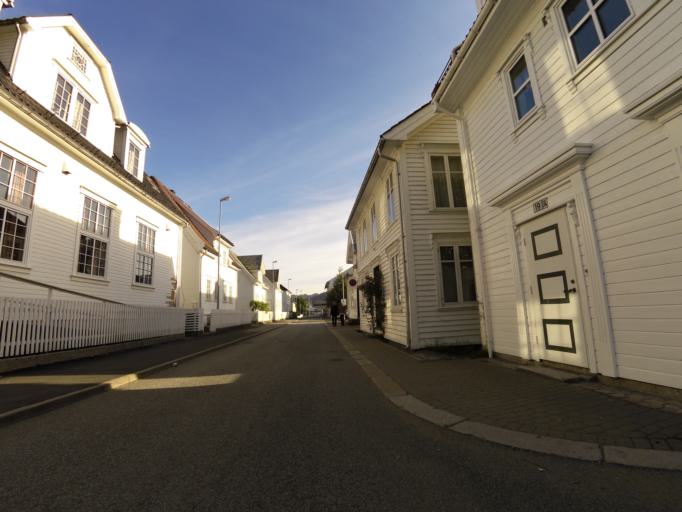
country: NO
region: Vest-Agder
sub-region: Flekkefjord
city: Flekkefjord
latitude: 58.2959
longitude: 6.6644
